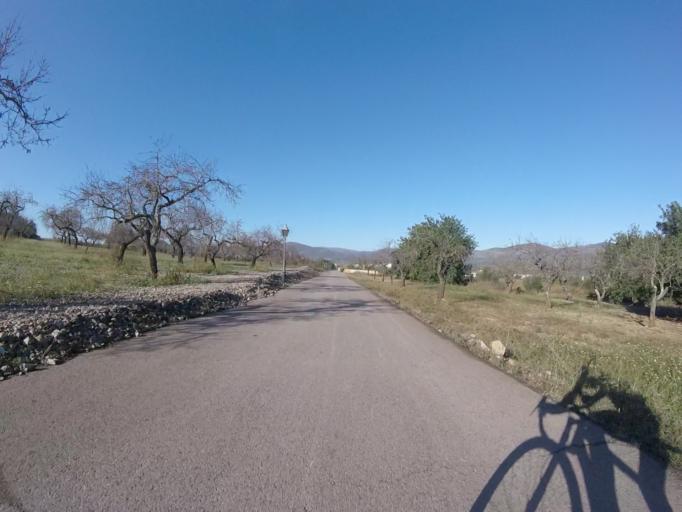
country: ES
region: Valencia
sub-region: Provincia de Castello
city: Santa Magdalena de Pulpis
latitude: 40.3550
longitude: 0.3078
